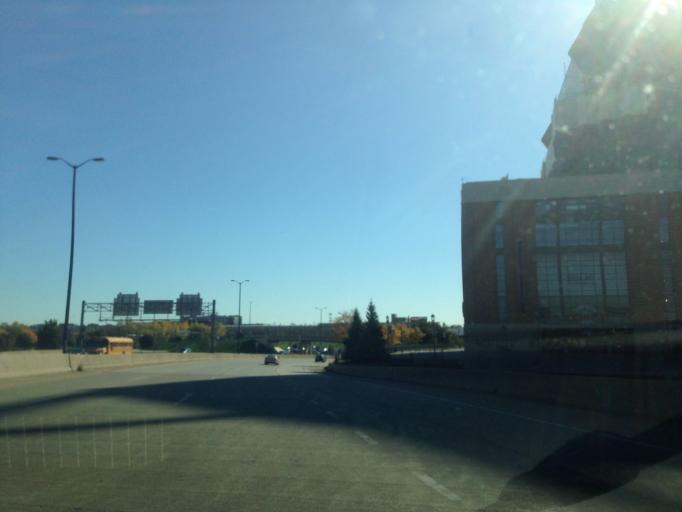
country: US
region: Wisconsin
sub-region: Milwaukee County
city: West Milwaukee
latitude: 43.0301
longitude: -87.9699
